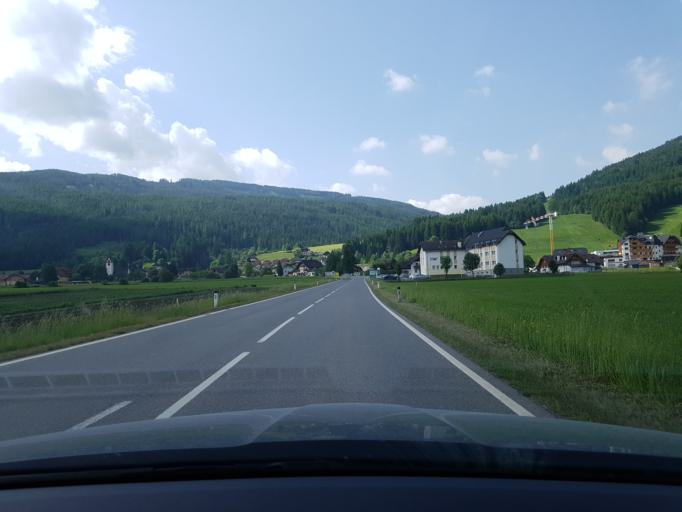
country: AT
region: Salzburg
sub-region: Politischer Bezirk Tamsweg
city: Sankt Margarethen im Lungau
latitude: 47.0843
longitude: 13.6924
